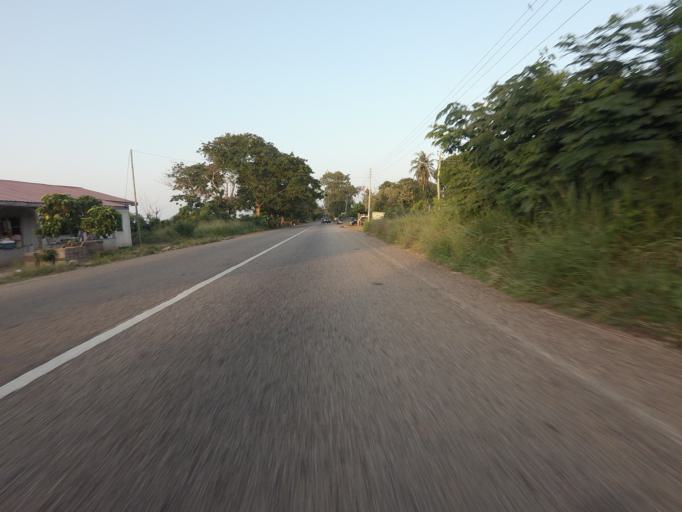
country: GH
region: Volta
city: Anloga
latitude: 5.7904
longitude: 0.8696
